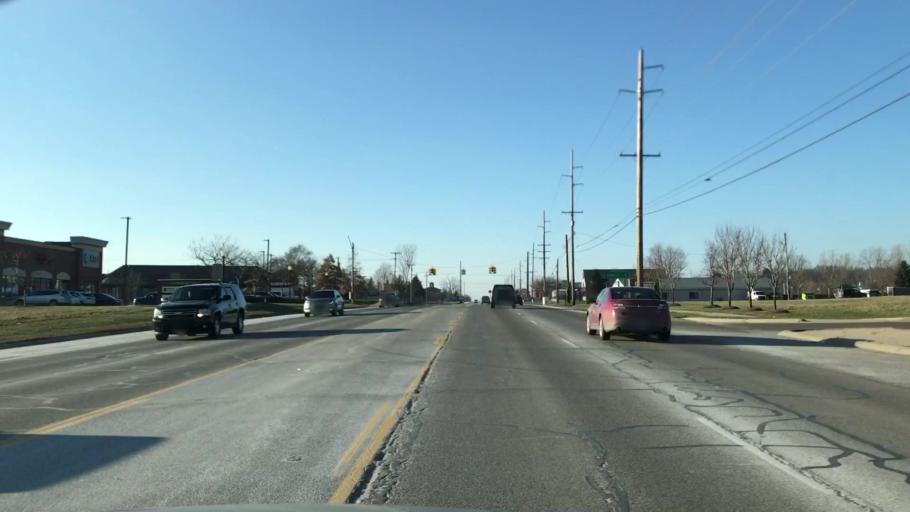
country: US
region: Michigan
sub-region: Livingston County
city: Howell
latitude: 42.5820
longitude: -83.8609
